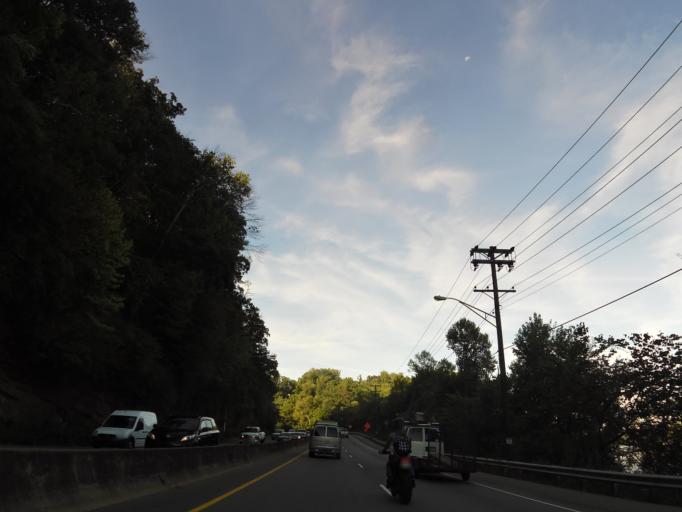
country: US
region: Tennessee
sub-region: Knox County
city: Knoxville
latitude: 35.9283
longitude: -83.9519
